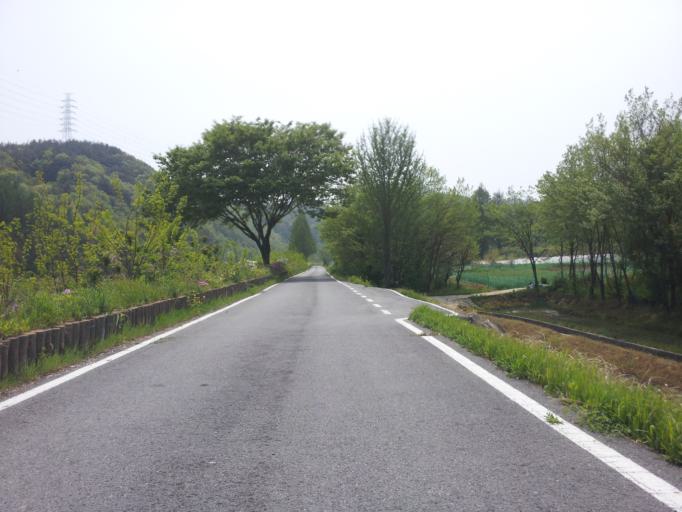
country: KR
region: Daejeon
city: Daejeon
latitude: 36.2613
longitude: 127.2950
